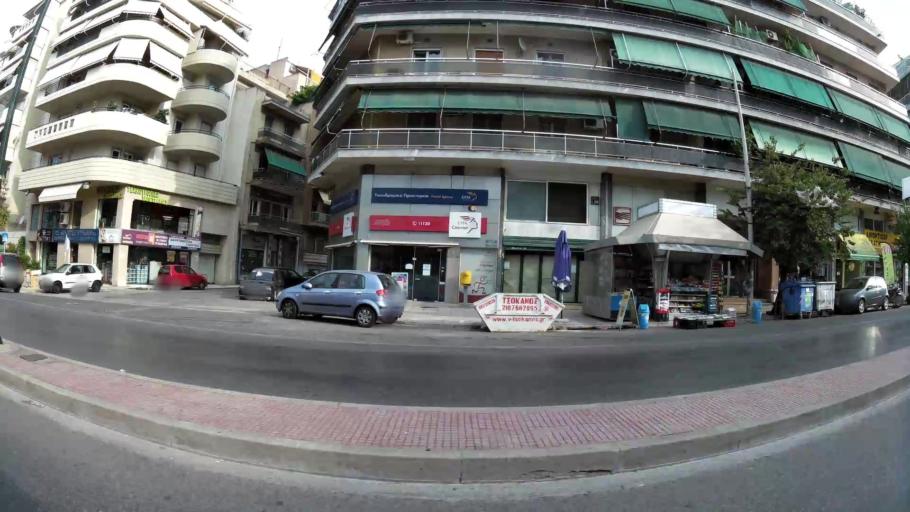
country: GR
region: Attica
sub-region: Nomarchia Athinas
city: Nea Chalkidona
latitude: 38.0133
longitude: 23.7226
